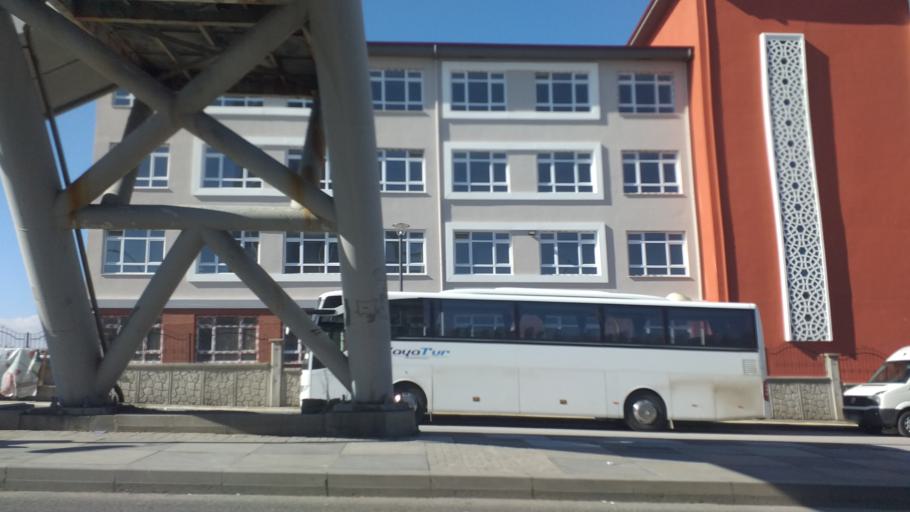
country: TR
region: Ankara
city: Ankara
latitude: 39.9050
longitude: 32.8142
